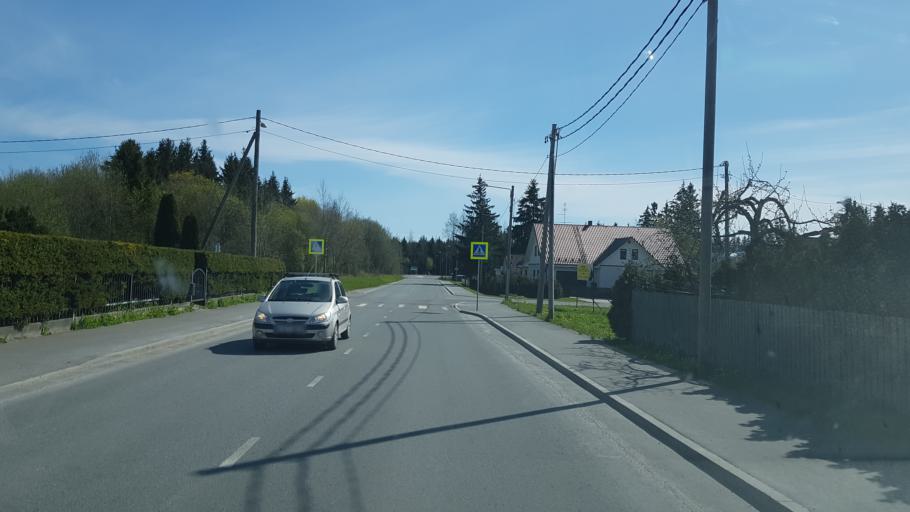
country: EE
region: Harju
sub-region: Keila linn
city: Keila
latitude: 59.3012
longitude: 24.4256
